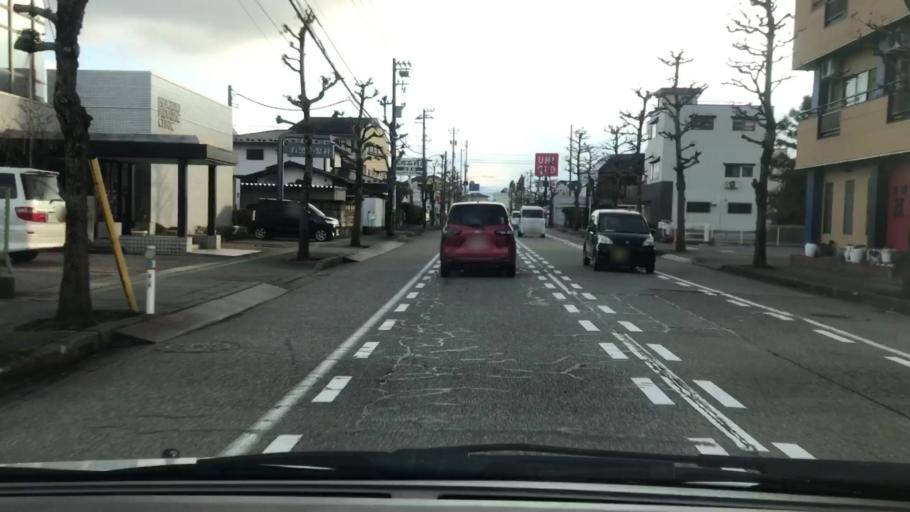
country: JP
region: Toyama
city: Toyama-shi
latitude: 36.6717
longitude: 137.2370
